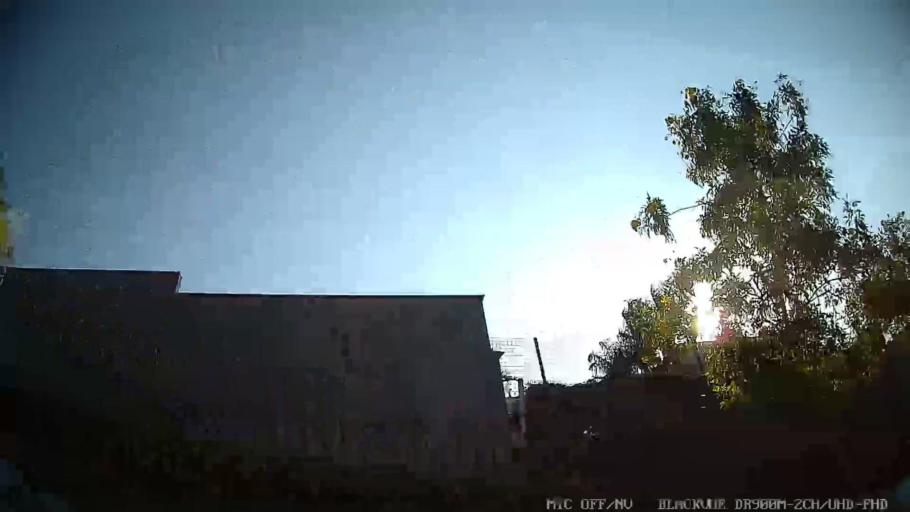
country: BR
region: Sao Paulo
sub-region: Itatiba
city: Itatiba
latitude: -22.9881
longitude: -46.8394
